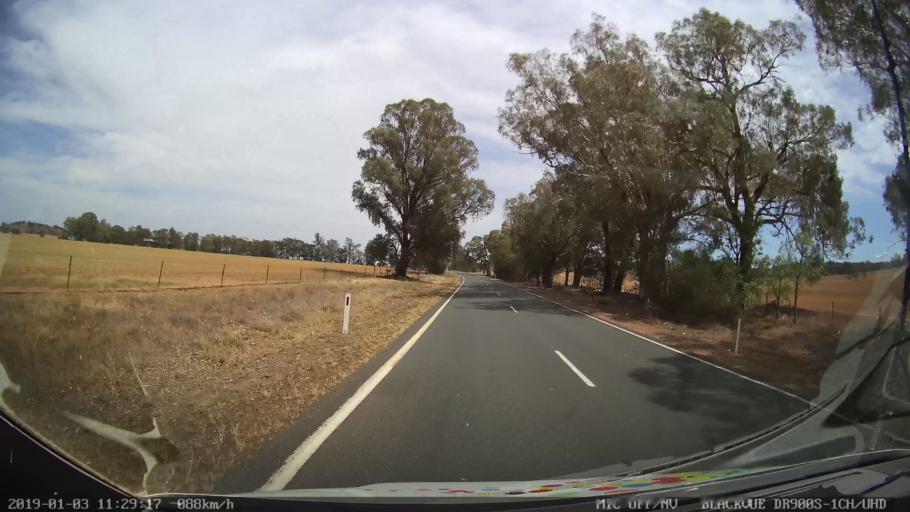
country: AU
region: New South Wales
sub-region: Weddin
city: Grenfell
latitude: -33.9938
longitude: 148.2001
